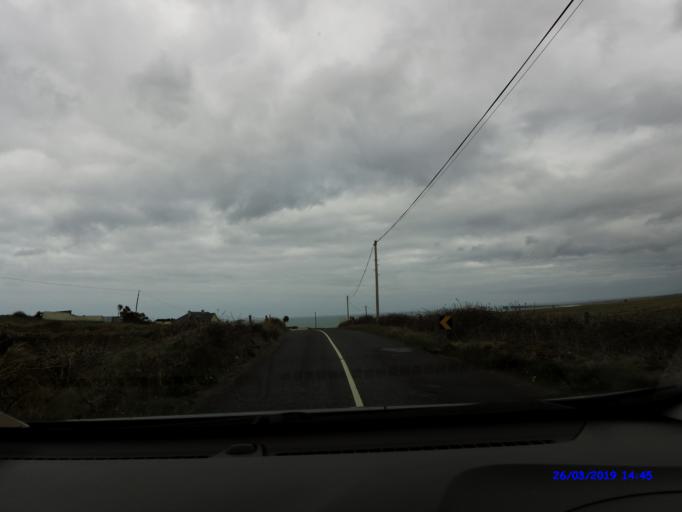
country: IE
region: Connaught
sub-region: Maigh Eo
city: Crossmolina
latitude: 54.3035
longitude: -9.4239
